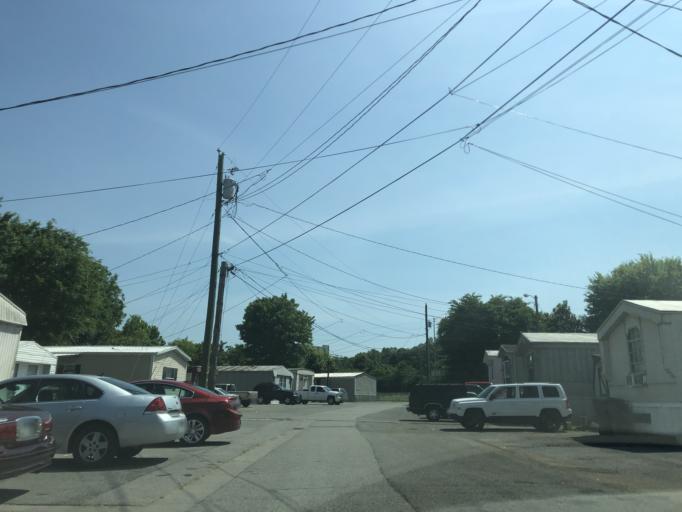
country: US
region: Tennessee
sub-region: Davidson County
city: Nashville
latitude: 36.2015
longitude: -86.7782
